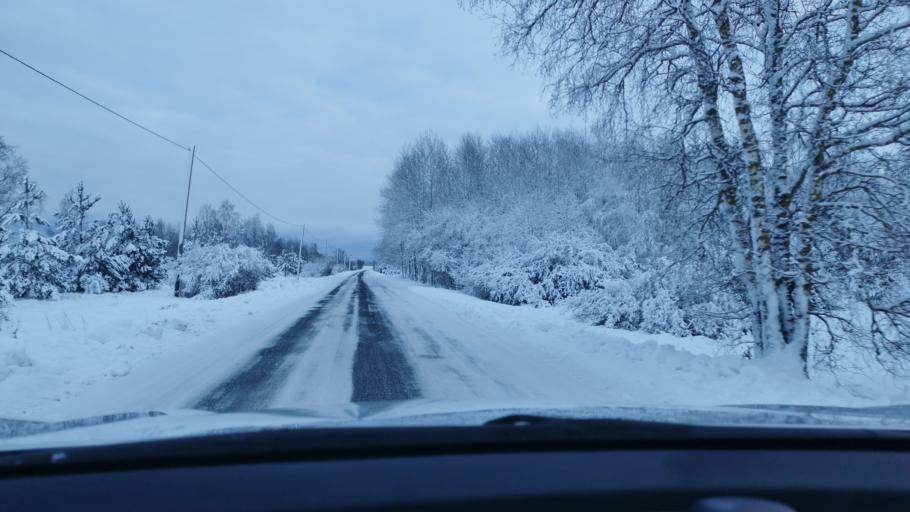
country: EE
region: Laeaene-Virumaa
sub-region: Viru-Nigula vald
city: Kunda
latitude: 59.4817
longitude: 26.5053
